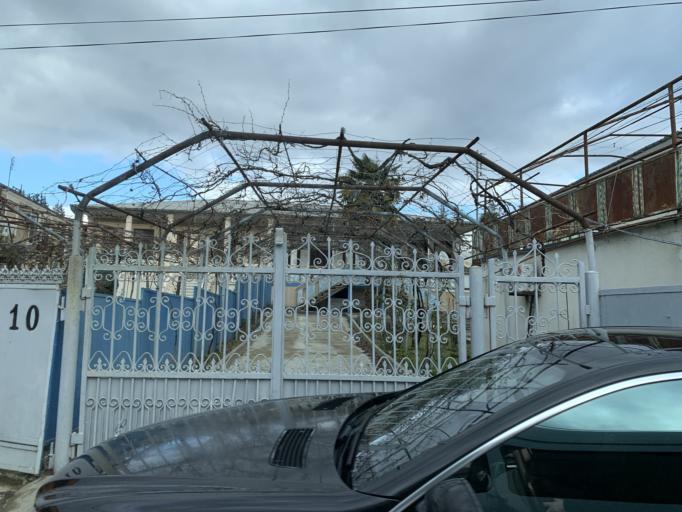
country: GE
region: Imereti
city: Tsqaltubo
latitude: 42.3306
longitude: 42.5978
